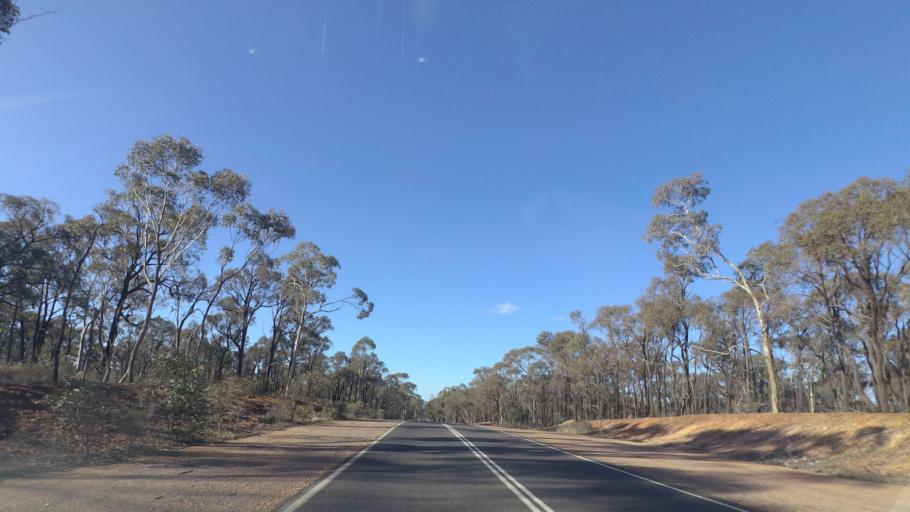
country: AU
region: Victoria
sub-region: Greater Bendigo
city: Epsom
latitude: -36.6667
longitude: 144.4340
